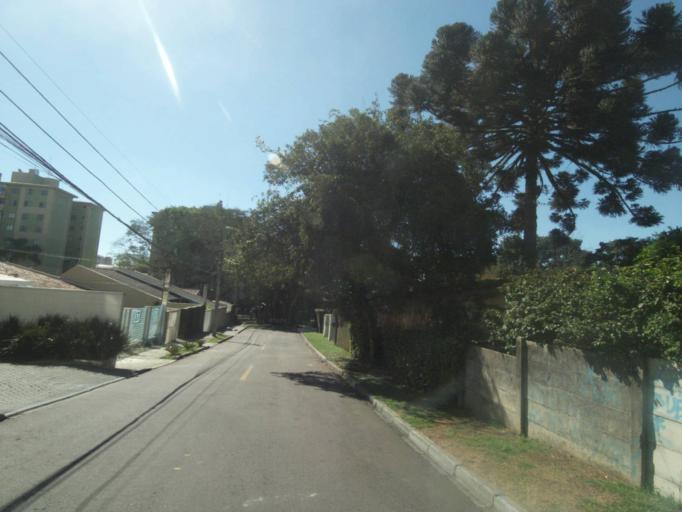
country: BR
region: Parana
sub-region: Curitiba
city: Curitiba
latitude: -25.3937
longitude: -49.2310
